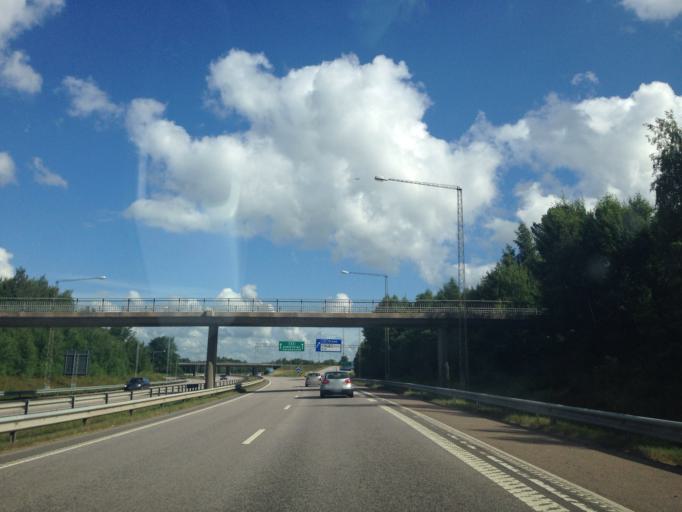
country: SE
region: Kalmar
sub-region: Kalmar Kommun
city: Kalmar
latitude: 56.6795
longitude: 16.3287
